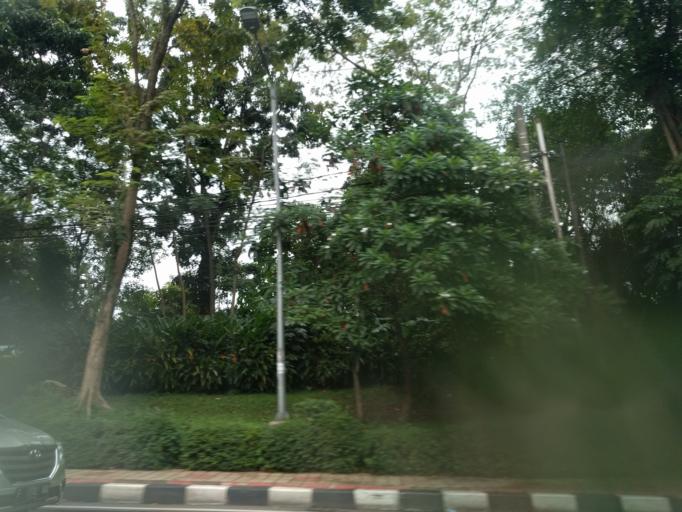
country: ID
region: West Java
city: Bogor
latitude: -6.5934
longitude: 106.7979
